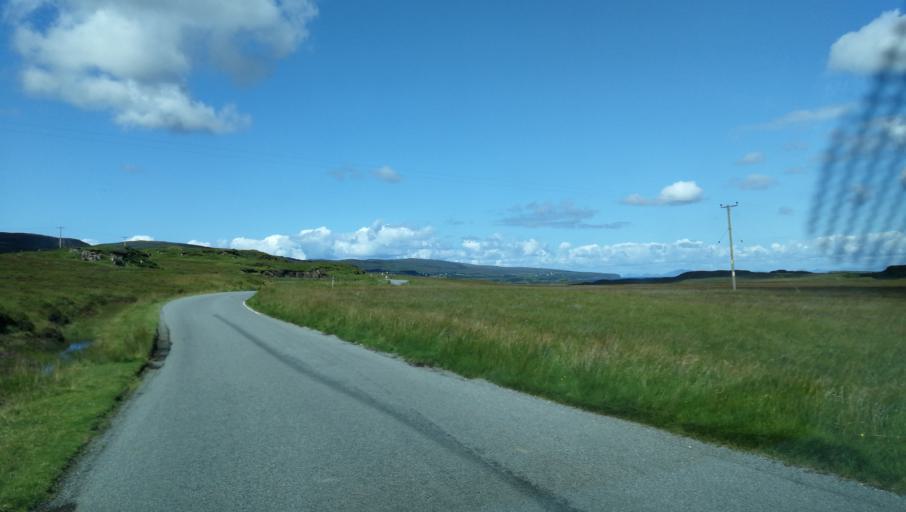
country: GB
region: Scotland
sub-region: Highland
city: Isle of Skye
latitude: 57.4253
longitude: -6.5993
